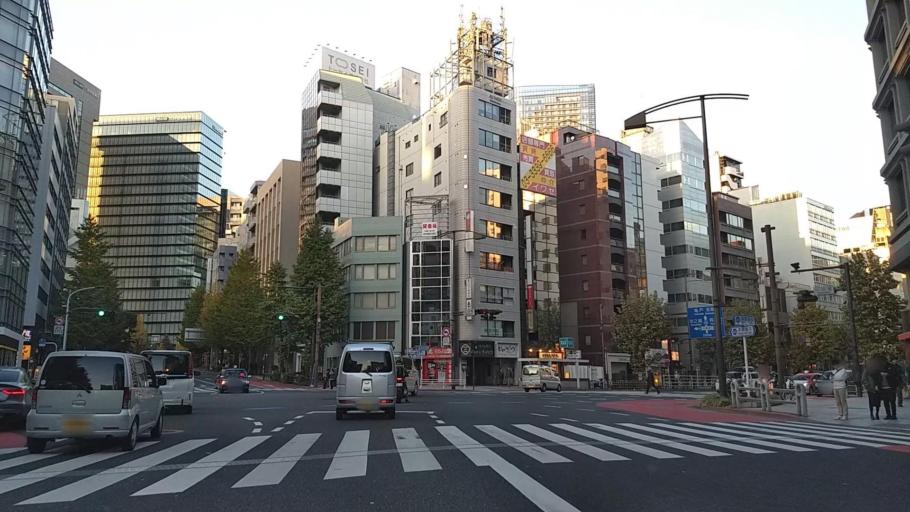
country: JP
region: Tokyo
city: Tokyo
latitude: 35.6943
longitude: 139.7653
